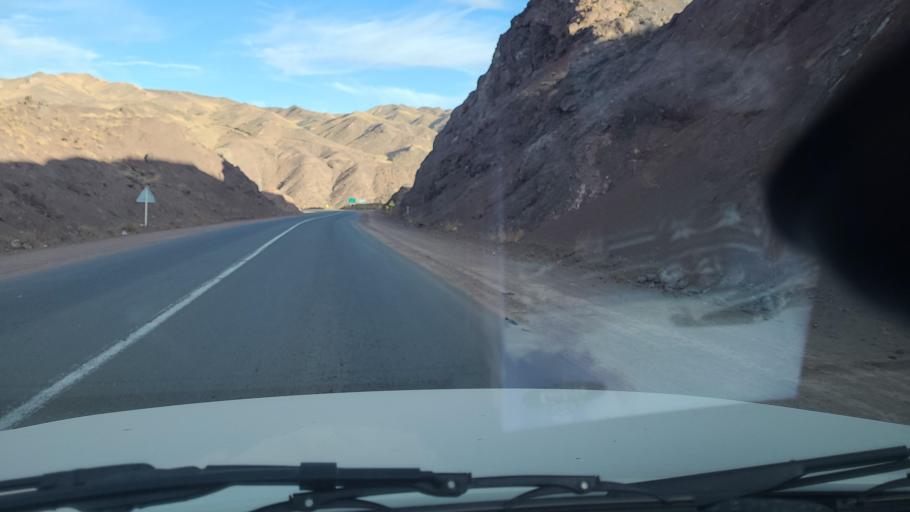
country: IR
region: Razavi Khorasan
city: Sabzevar
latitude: 36.4184
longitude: 57.5617
